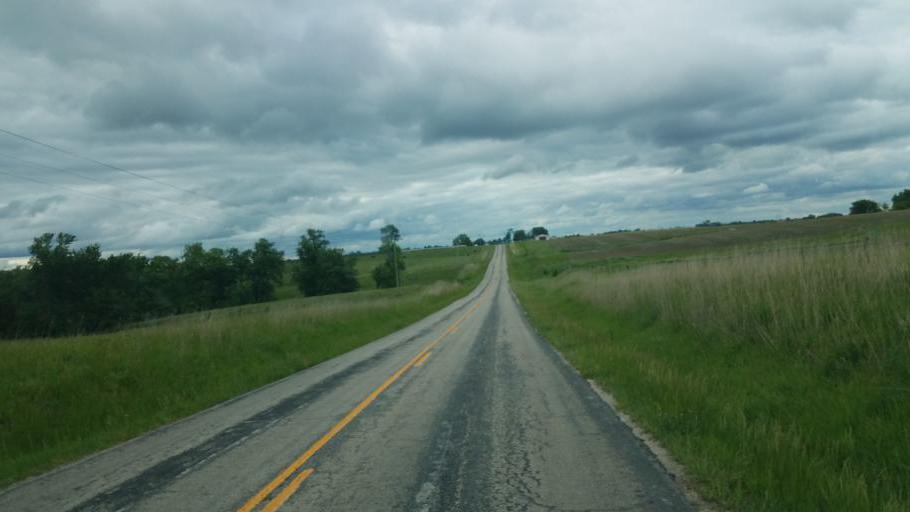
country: US
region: Missouri
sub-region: Mercer County
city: Princeton
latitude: 40.3574
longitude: -93.6806
